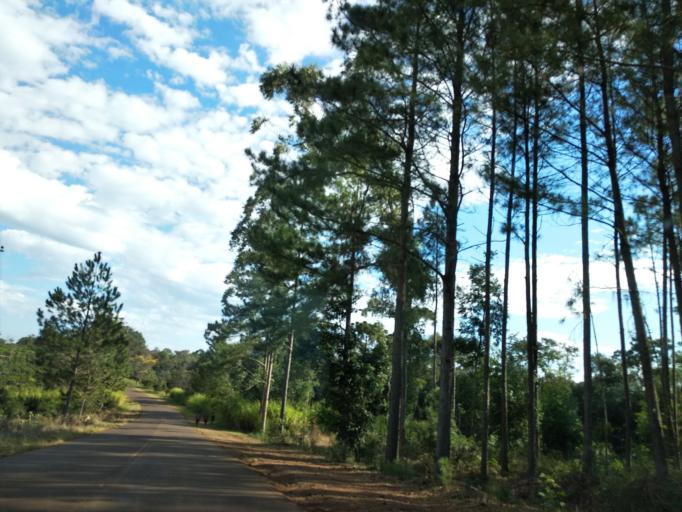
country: AR
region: Misiones
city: Aristobulo del Valle
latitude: -27.0708
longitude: -54.8291
